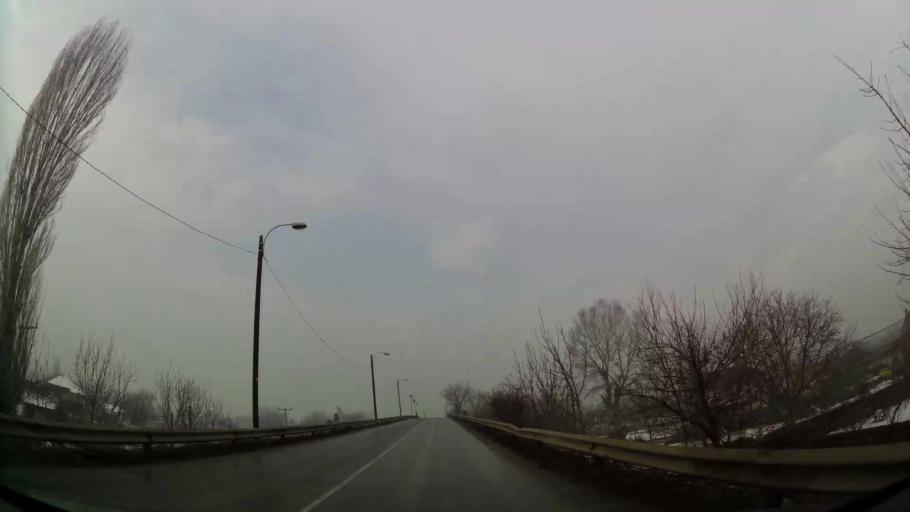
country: MK
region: Ilinden
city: Jurumleri
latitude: 41.9696
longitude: 21.5459
